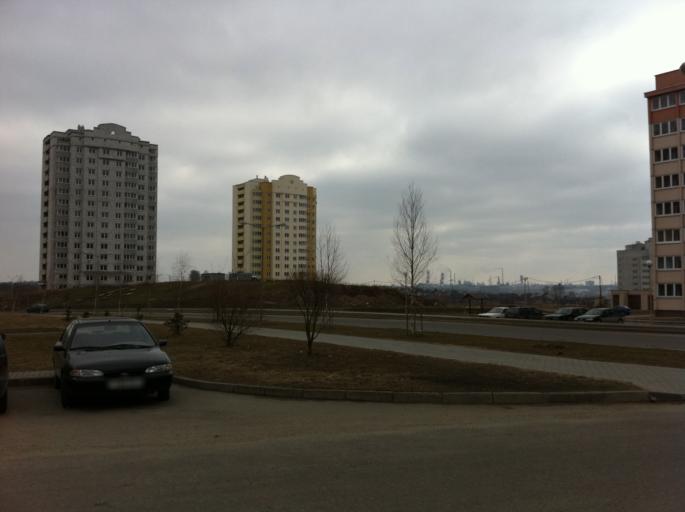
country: BY
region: Grodnenskaya
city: Hrodna
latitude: 53.7107
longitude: 23.8564
